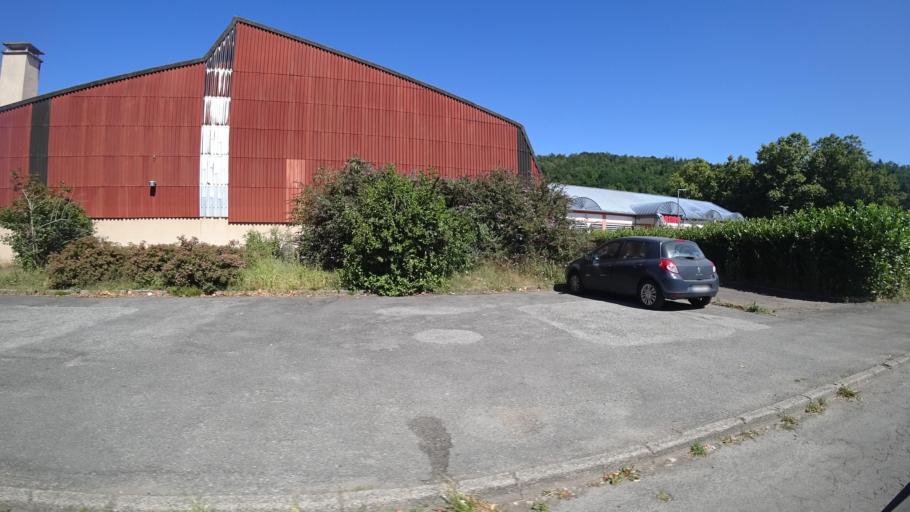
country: FR
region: Midi-Pyrenees
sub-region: Departement de l'Aveyron
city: Cransac
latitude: 44.5254
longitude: 2.2782
